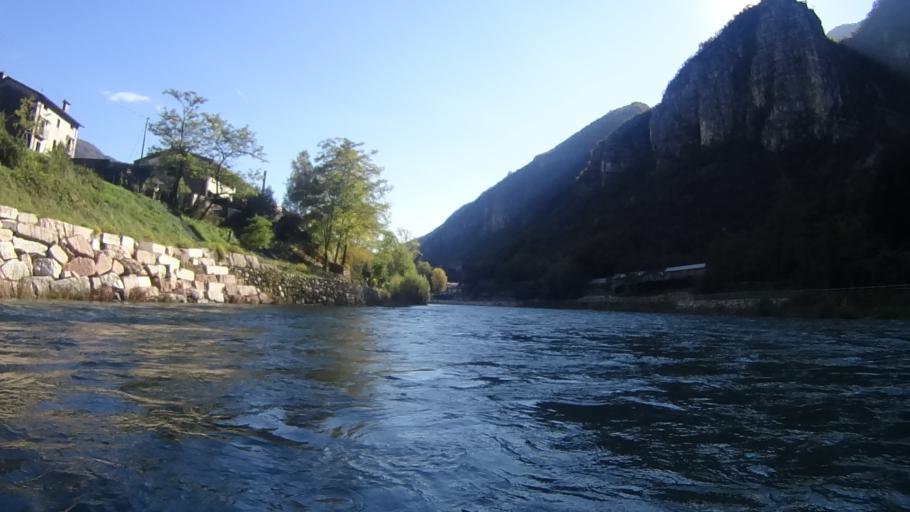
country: IT
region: Veneto
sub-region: Provincia di Vicenza
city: Valstagna
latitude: 45.8438
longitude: 11.6752
